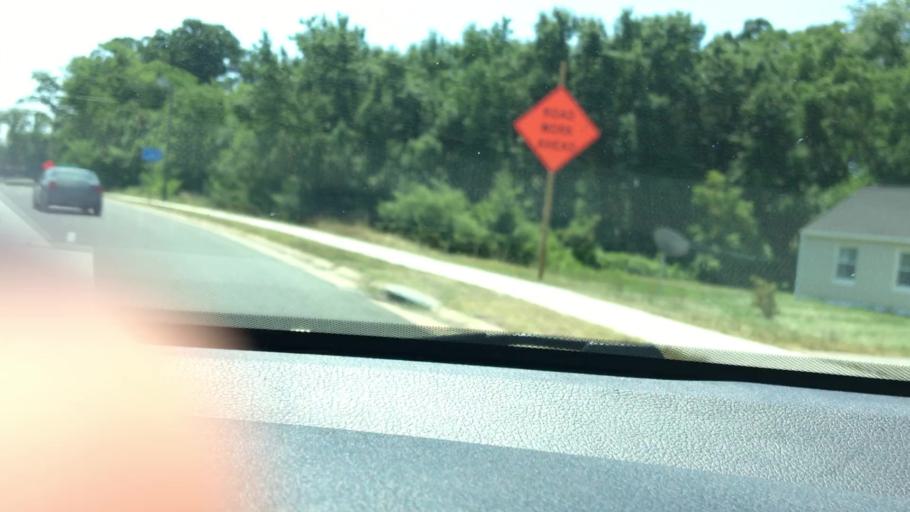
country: US
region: Virginia
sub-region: Prince William County
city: Lake Ridge
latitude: 38.6709
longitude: -77.3365
